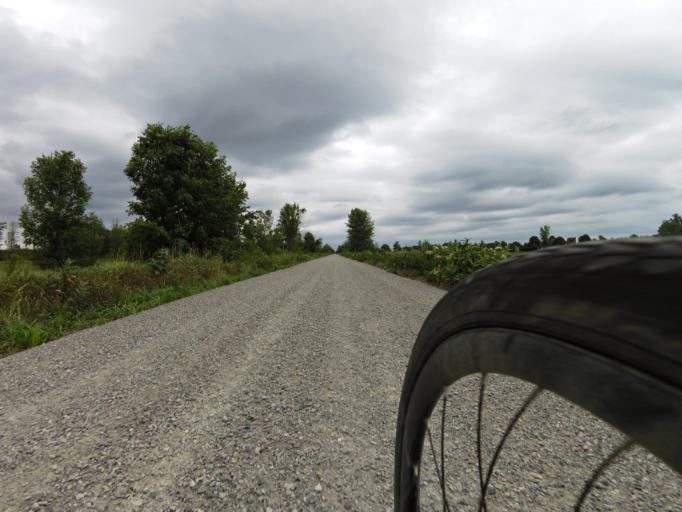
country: CA
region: Ontario
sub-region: Lanark County
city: Smiths Falls
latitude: 44.9245
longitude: -76.0310
